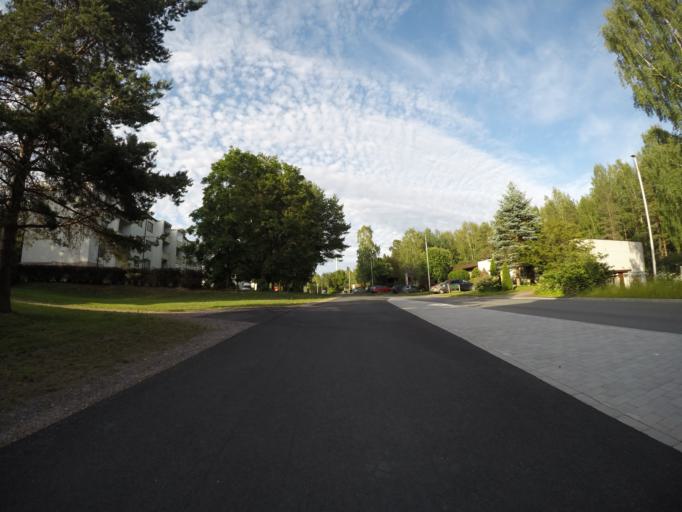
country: FI
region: Haeme
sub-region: Haemeenlinna
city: Haemeenlinna
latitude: 60.9823
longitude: 24.4063
